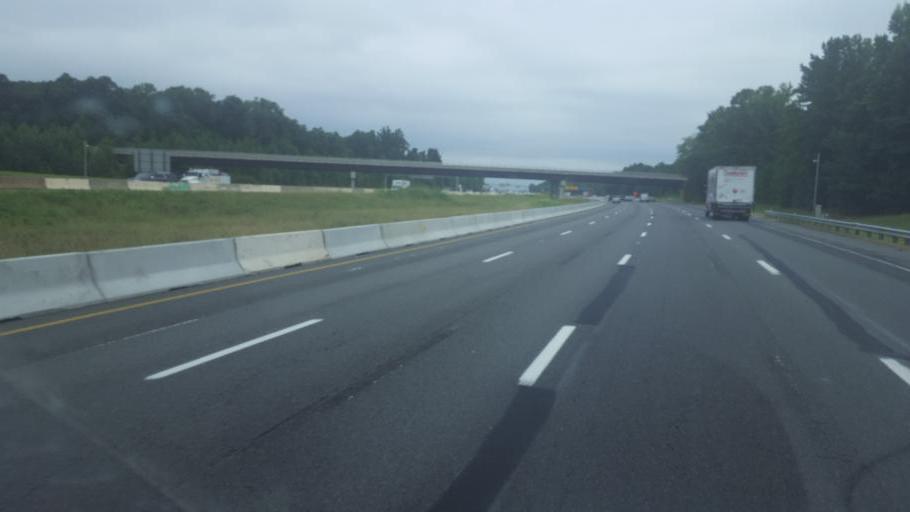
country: US
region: North Carolina
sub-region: Mecklenburg County
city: Huntersville
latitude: 35.3662
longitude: -80.8421
